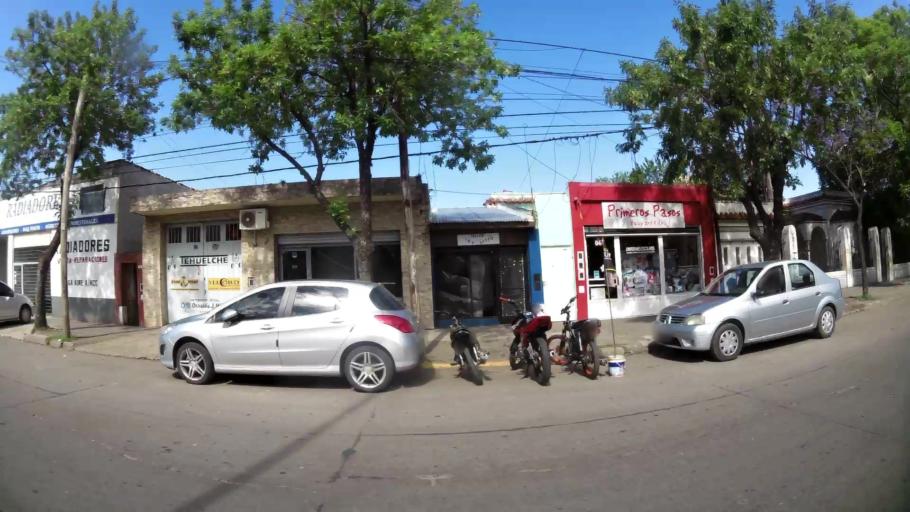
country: AR
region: Santa Fe
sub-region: Departamento de Rosario
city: Rosario
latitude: -32.9376
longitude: -60.7127
